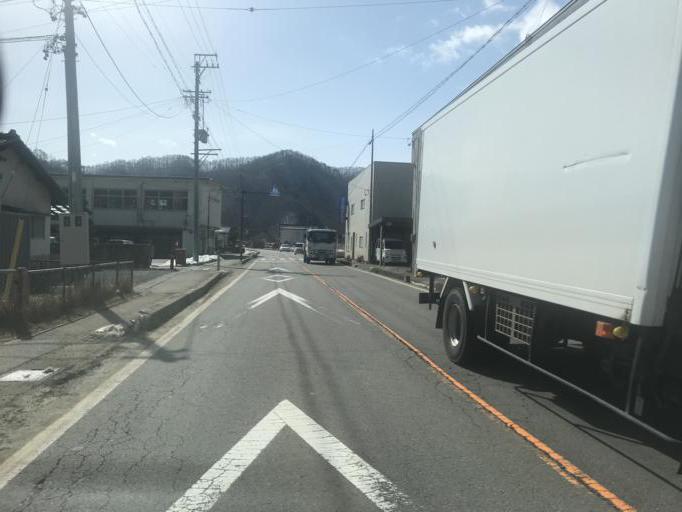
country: JP
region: Nagano
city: Saku
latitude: 36.0220
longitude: 138.4907
